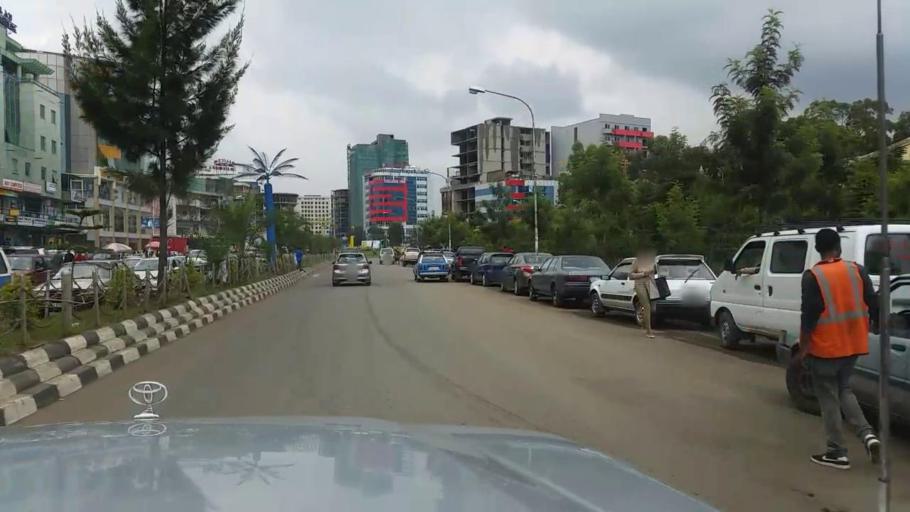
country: ET
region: Adis Abeba
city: Addis Ababa
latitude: 8.9967
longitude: 38.7877
